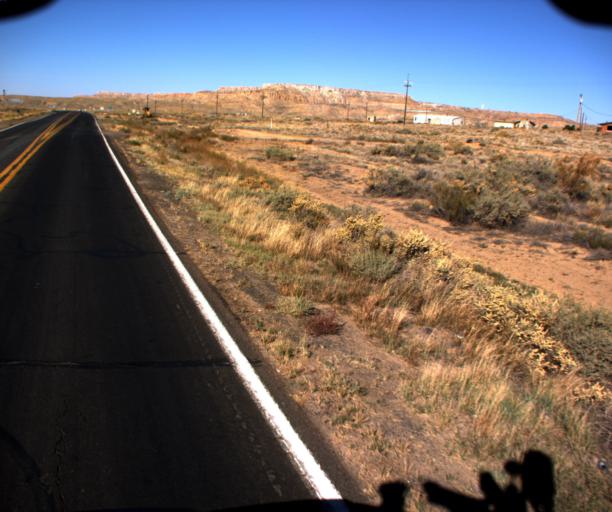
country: US
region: Arizona
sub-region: Navajo County
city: First Mesa
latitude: 35.7927
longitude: -110.4936
